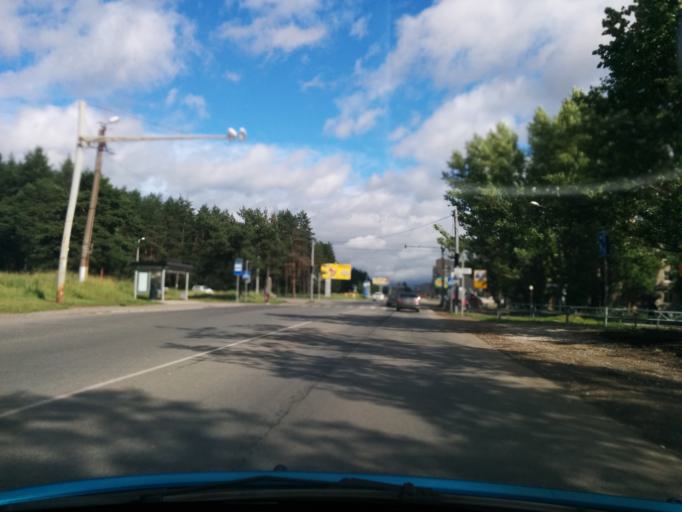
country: RU
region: Perm
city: Kondratovo
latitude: 58.0391
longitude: 56.1333
